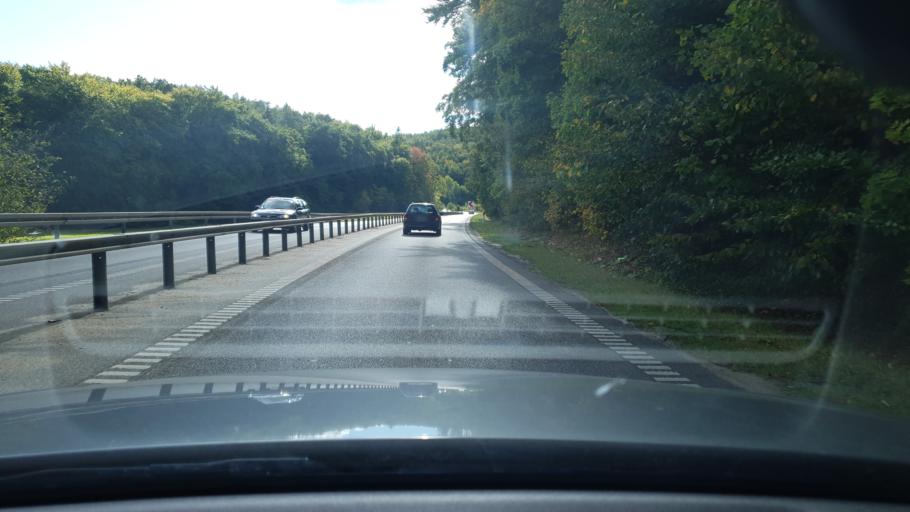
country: PL
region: Pomeranian Voivodeship
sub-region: Powiat wejherowski
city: Reda
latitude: 54.6248
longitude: 18.3407
